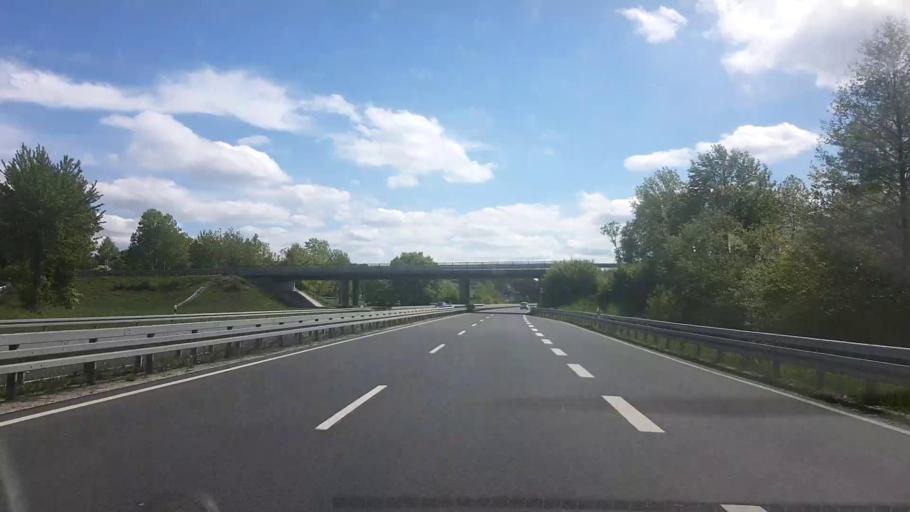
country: DE
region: Bavaria
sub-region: Upper Franconia
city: Niederfullbach
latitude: 50.2242
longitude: 10.9807
